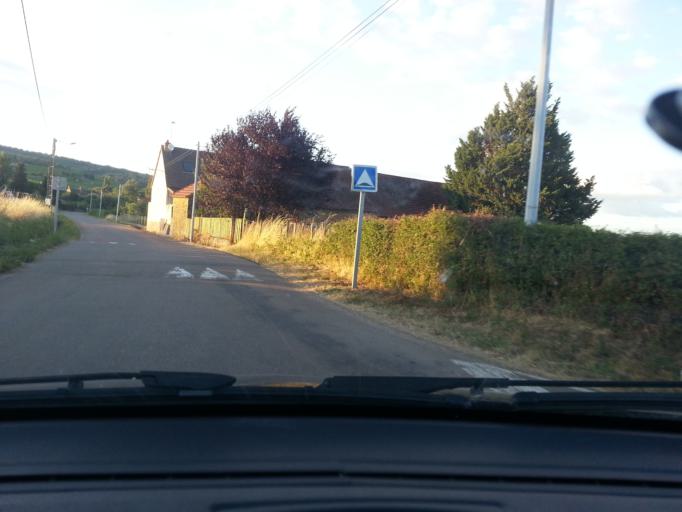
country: FR
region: Bourgogne
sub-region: Departement de Saone-et-Loire
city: Givry
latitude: 46.7608
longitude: 4.7181
